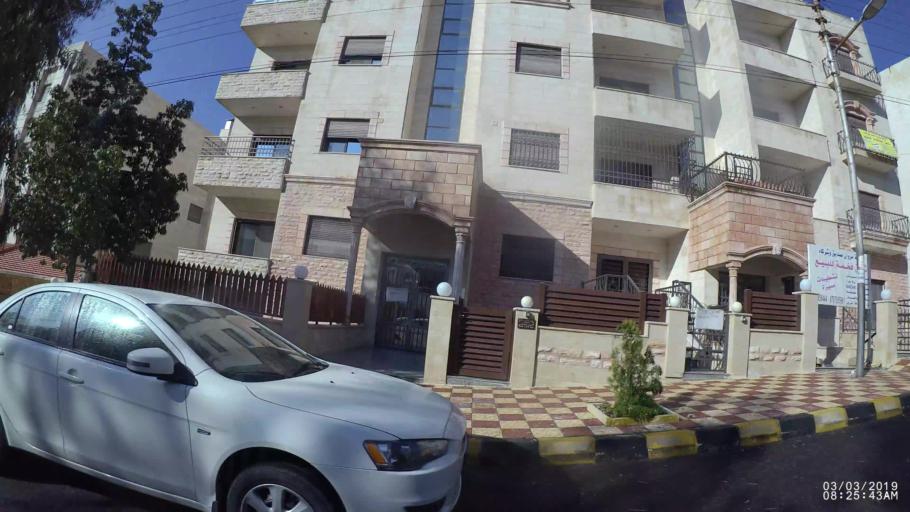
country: JO
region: Amman
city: Al Jubayhah
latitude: 31.9955
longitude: 35.8900
